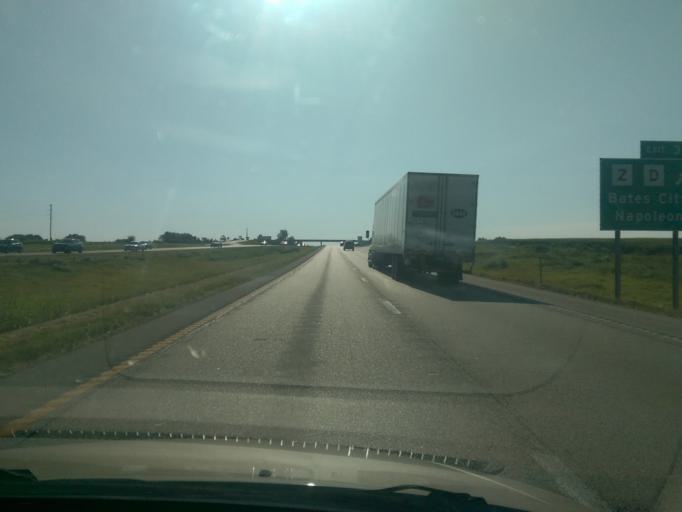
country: US
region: Missouri
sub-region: Jackson County
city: Oak Grove
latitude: 39.0114
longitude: -94.0632
